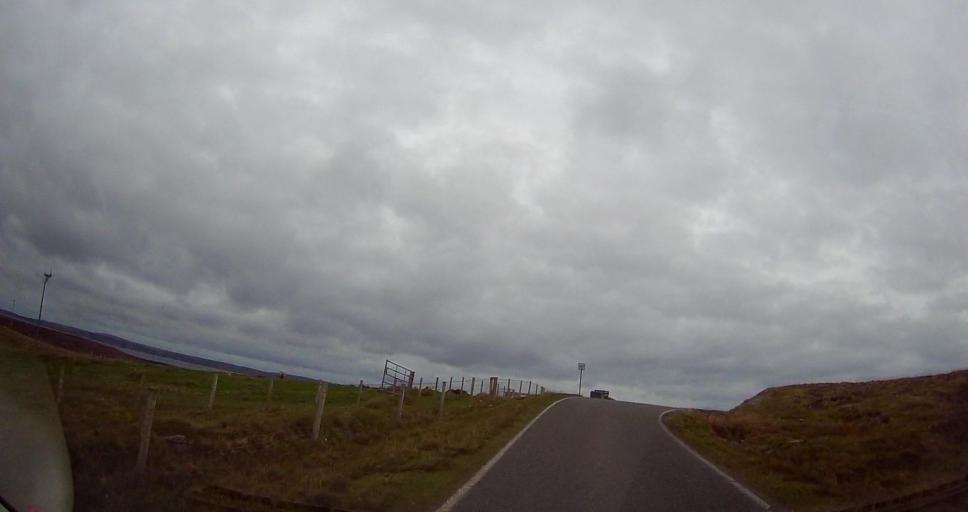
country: GB
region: Scotland
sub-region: Shetland Islands
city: Shetland
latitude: 60.5454
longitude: -1.0573
